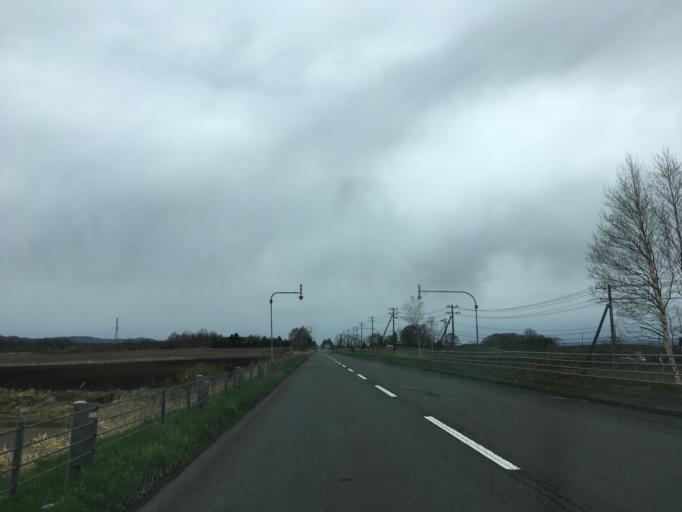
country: JP
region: Hokkaido
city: Chitose
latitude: 42.9085
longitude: 141.8118
